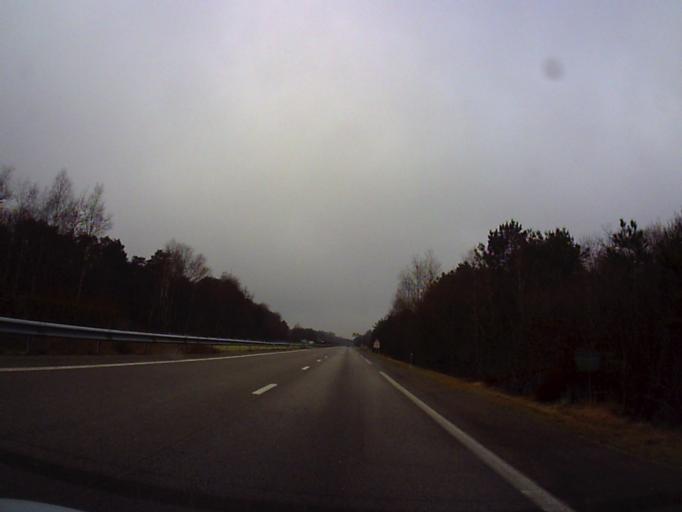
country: FR
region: Brittany
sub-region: Departement du Morbihan
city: Serent
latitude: 47.7647
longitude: -2.5078
